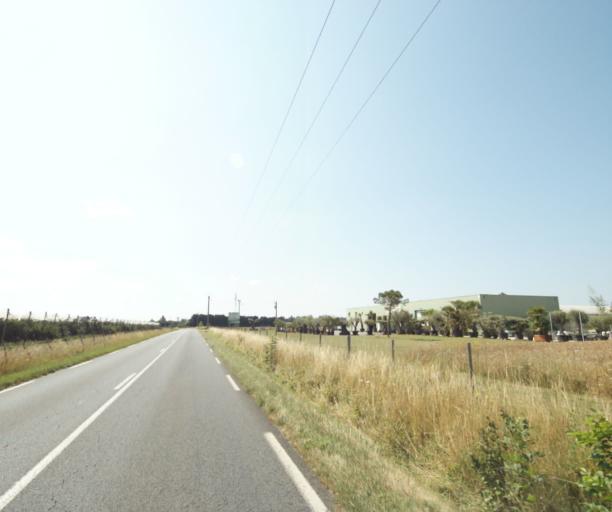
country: FR
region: Centre
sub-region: Departement du Loiret
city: Saint-Cyr-en-Val
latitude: 47.8469
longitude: 1.9569
